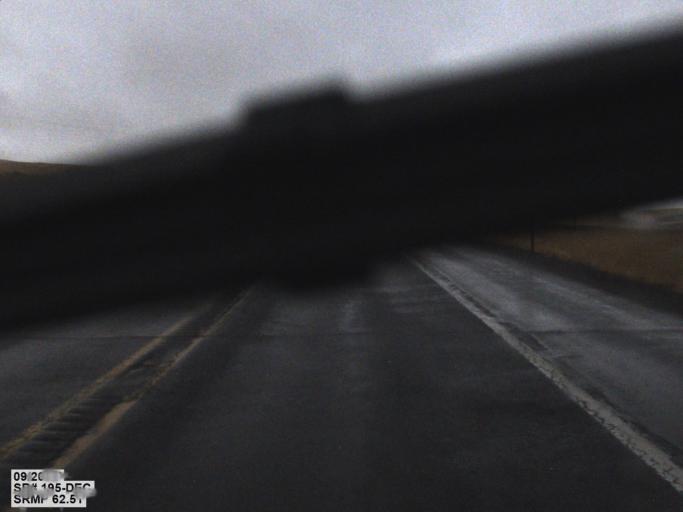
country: US
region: Washington
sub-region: Whitman County
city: Colfax
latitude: 47.2091
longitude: -117.3627
